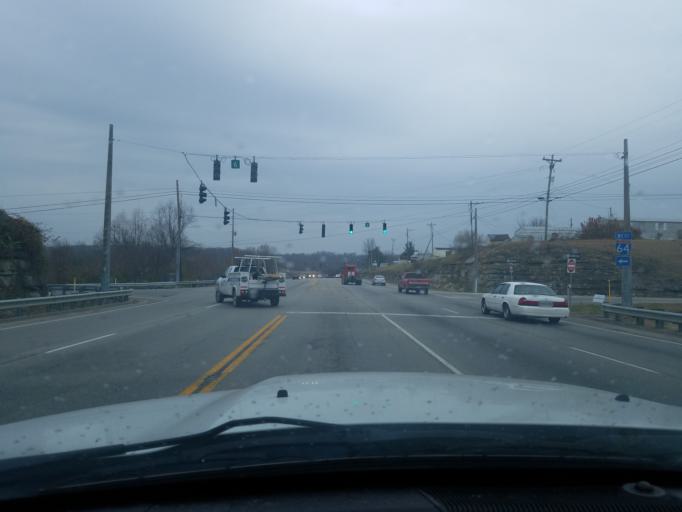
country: US
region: Kentucky
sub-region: Rowan County
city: Morehead
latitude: 38.1927
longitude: -83.4790
